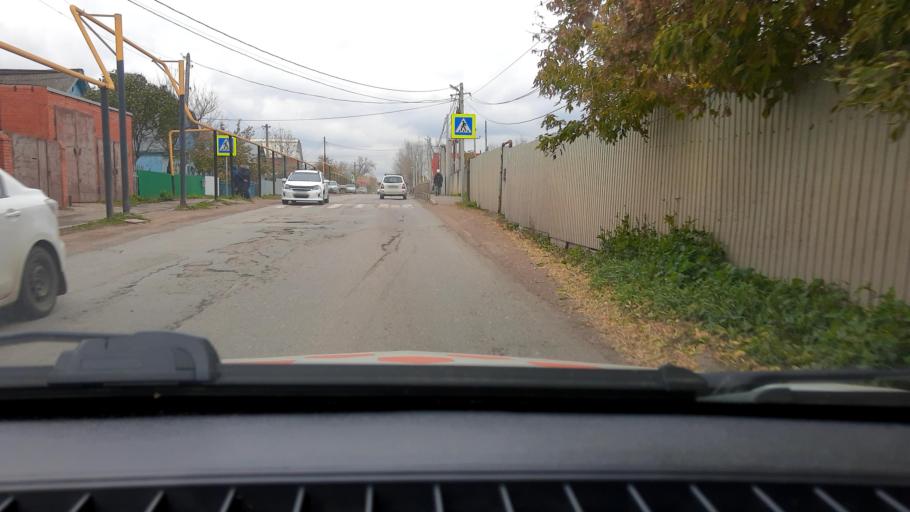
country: RU
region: Bashkortostan
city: Mikhaylovka
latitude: 54.6994
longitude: 55.8491
